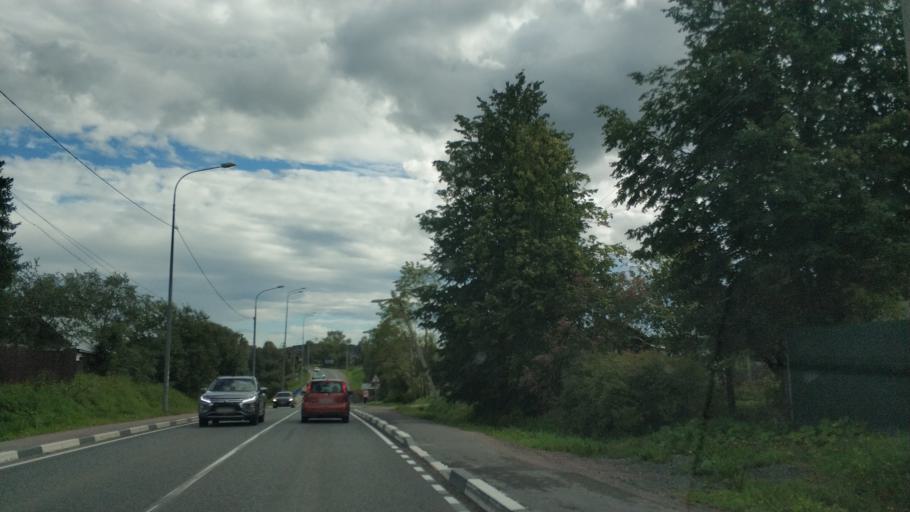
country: RU
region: Republic of Karelia
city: Khelyulya
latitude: 61.7498
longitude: 30.6632
